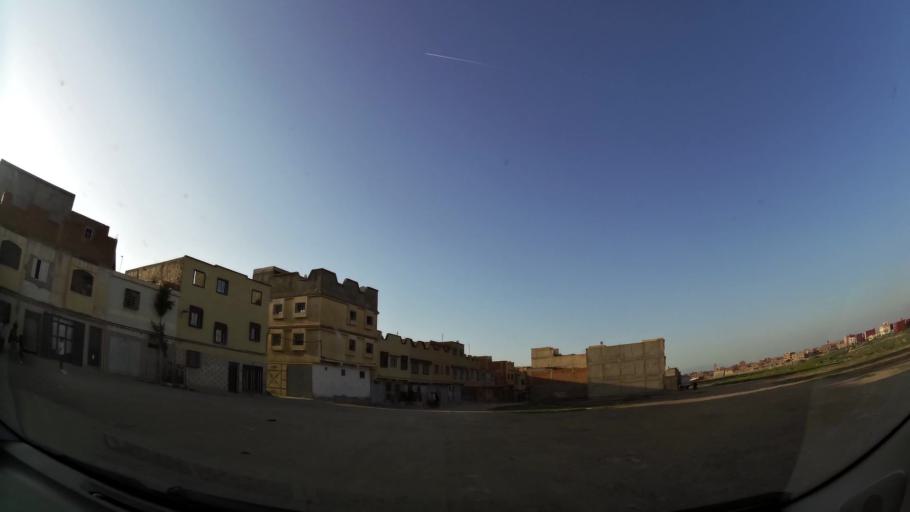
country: MA
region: Oriental
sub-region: Oujda-Angad
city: Oujda
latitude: 34.7067
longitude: -1.9070
